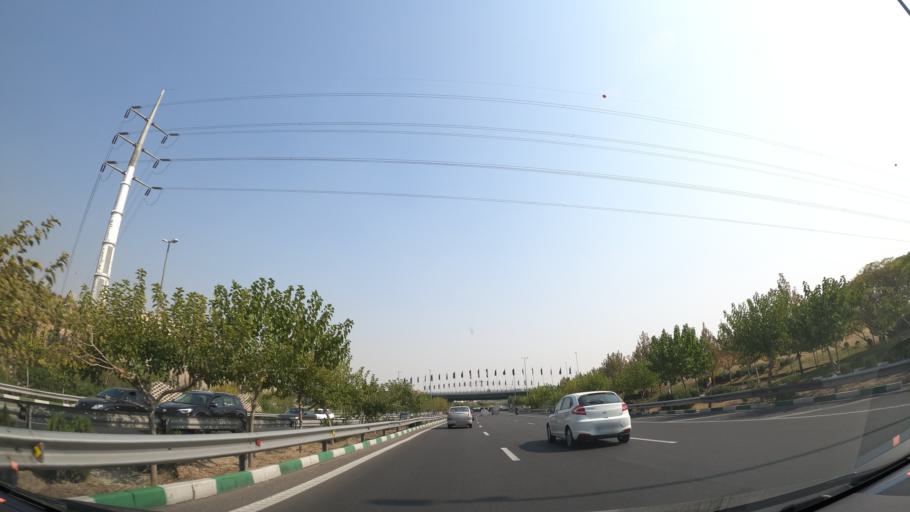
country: IR
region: Tehran
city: Shahr-e Qods
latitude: 35.7603
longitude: 51.2529
